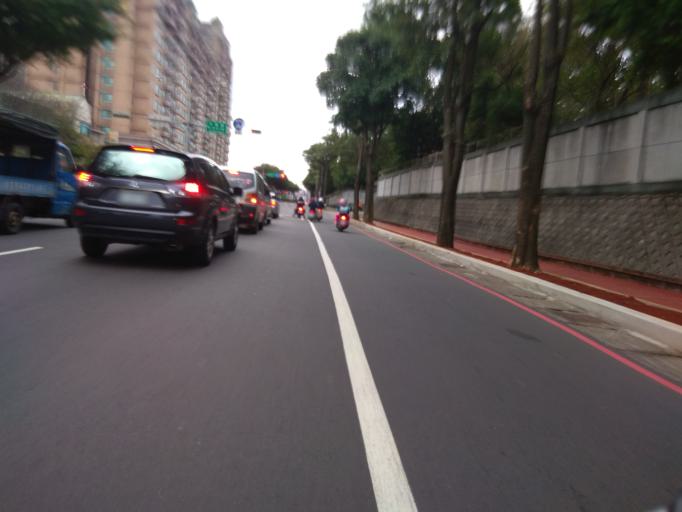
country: TW
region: Taiwan
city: Daxi
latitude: 24.9051
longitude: 121.2116
